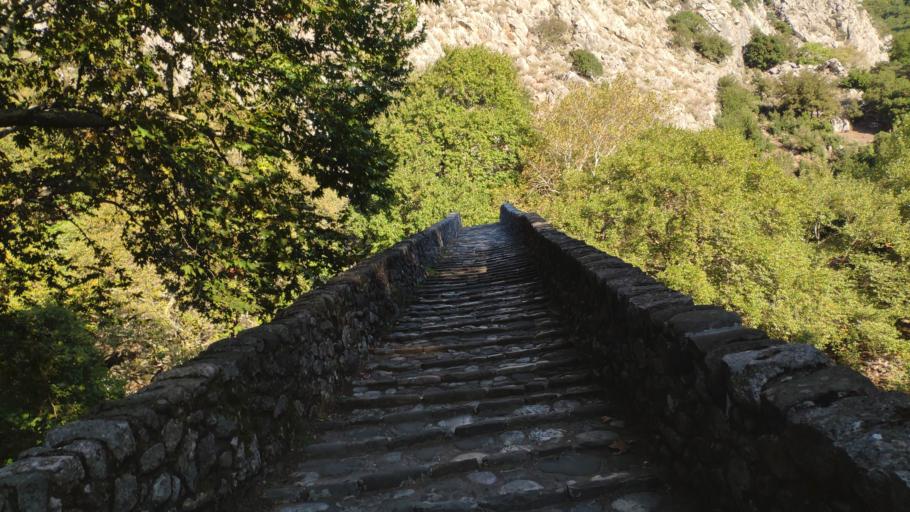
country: GR
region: Thessaly
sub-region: Trikala
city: Pyli
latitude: 39.4602
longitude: 21.6007
